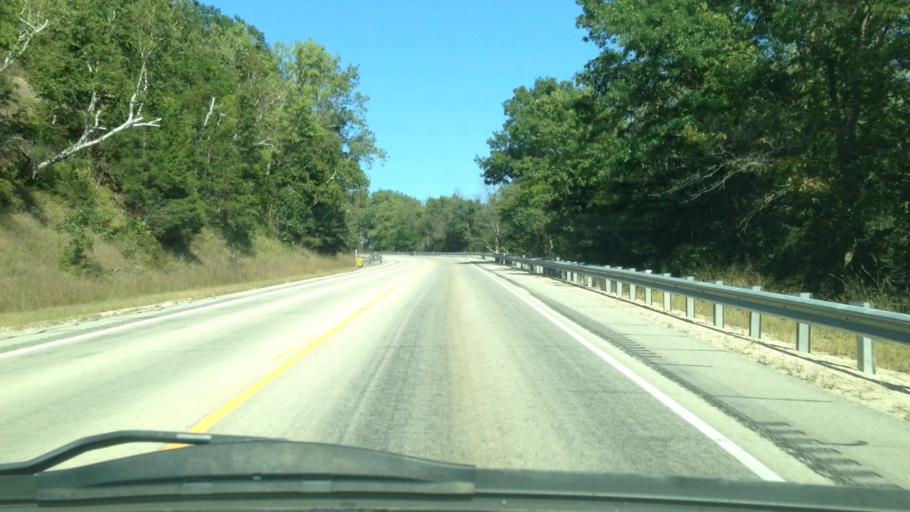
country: US
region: Minnesota
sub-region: Fillmore County
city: Rushford
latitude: 43.8363
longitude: -91.7591
